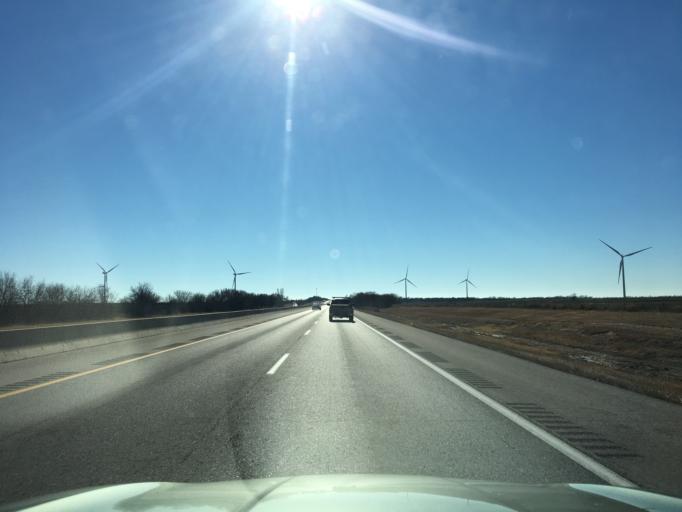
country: US
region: Kansas
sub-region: Sumner County
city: Wellington
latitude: 37.1428
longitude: -97.3394
